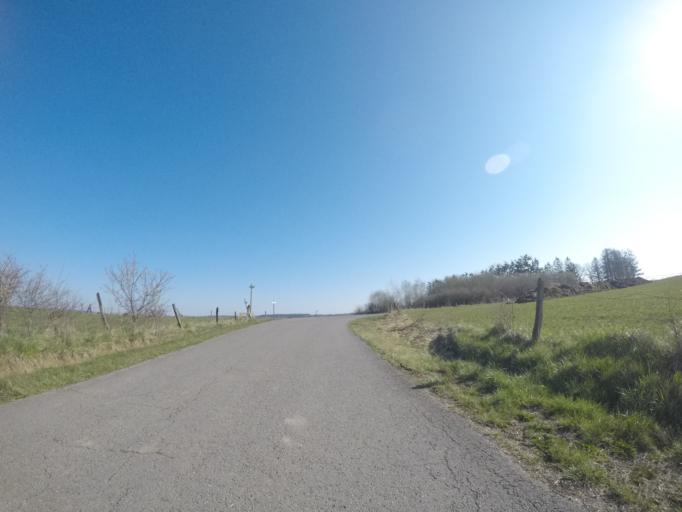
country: BE
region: Wallonia
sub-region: Province du Luxembourg
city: Habay-la-Vieille
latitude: 49.7134
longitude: 5.6163
